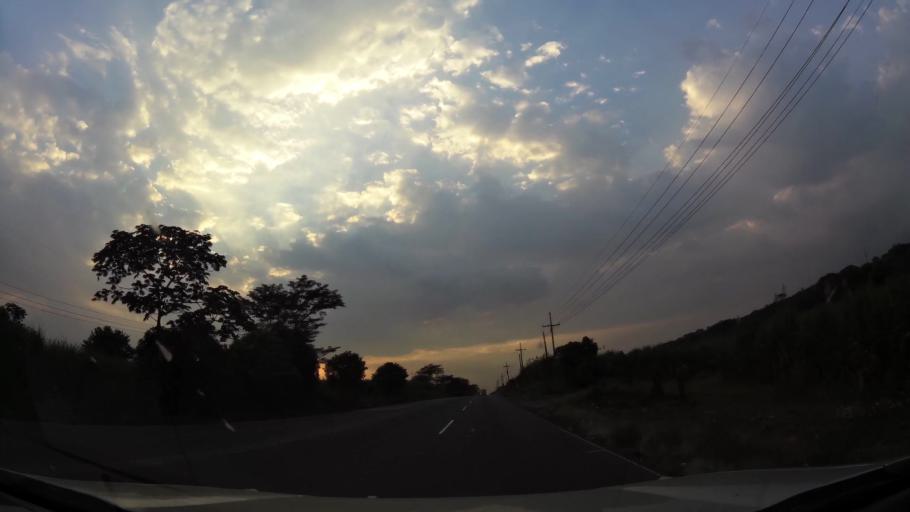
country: GT
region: Escuintla
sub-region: Municipio de Masagua
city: Masagua
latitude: 14.2675
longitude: -90.8781
